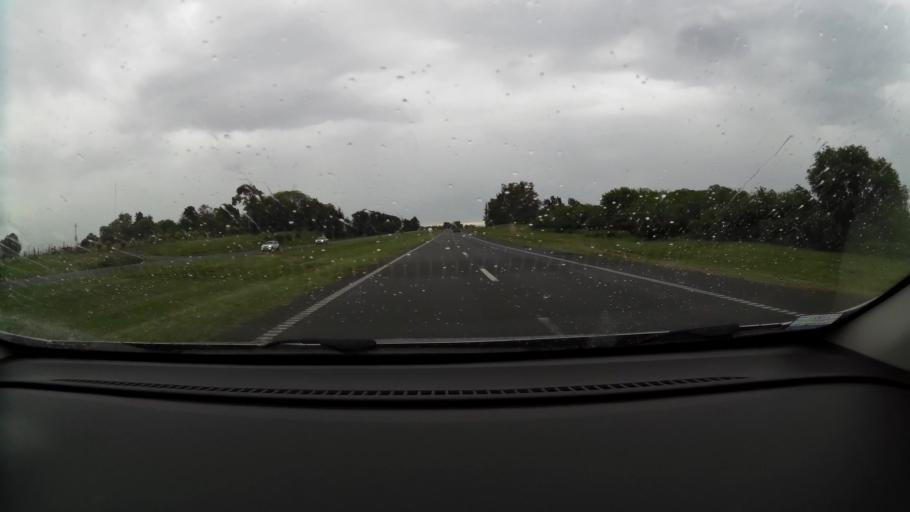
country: AR
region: Buenos Aires
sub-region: Partido de Baradero
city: Baradero
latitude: -33.8022
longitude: -59.6187
